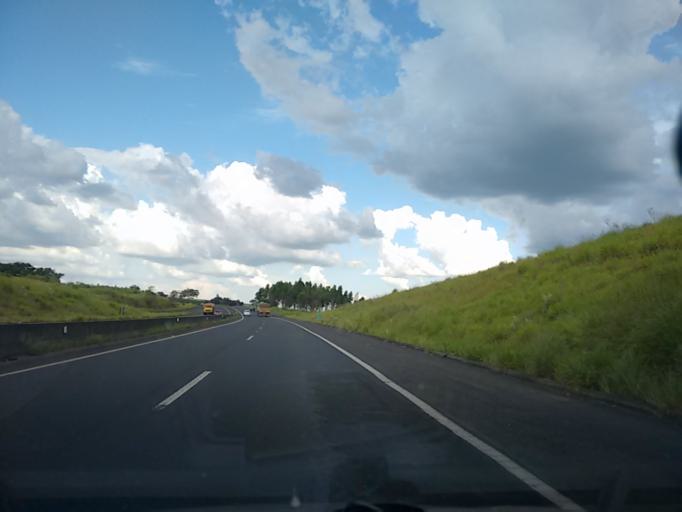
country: BR
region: Sao Paulo
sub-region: Garca
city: Garca
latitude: -22.2264
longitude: -49.7729
